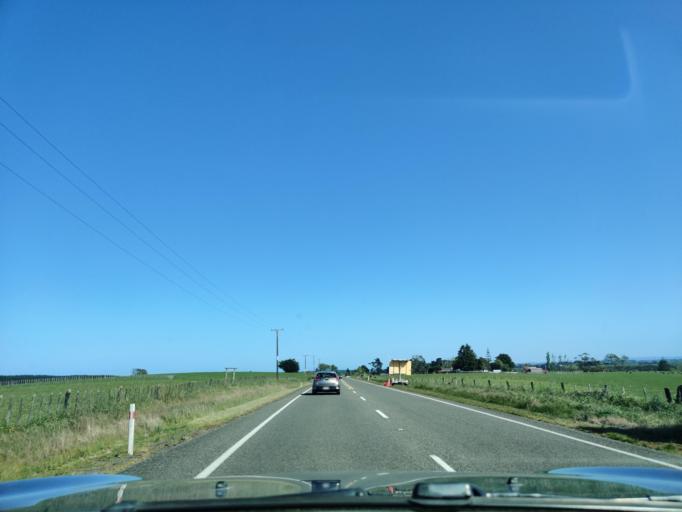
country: NZ
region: Manawatu-Wanganui
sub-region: Rangitikei District
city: Bulls
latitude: -40.0807
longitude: 175.2462
